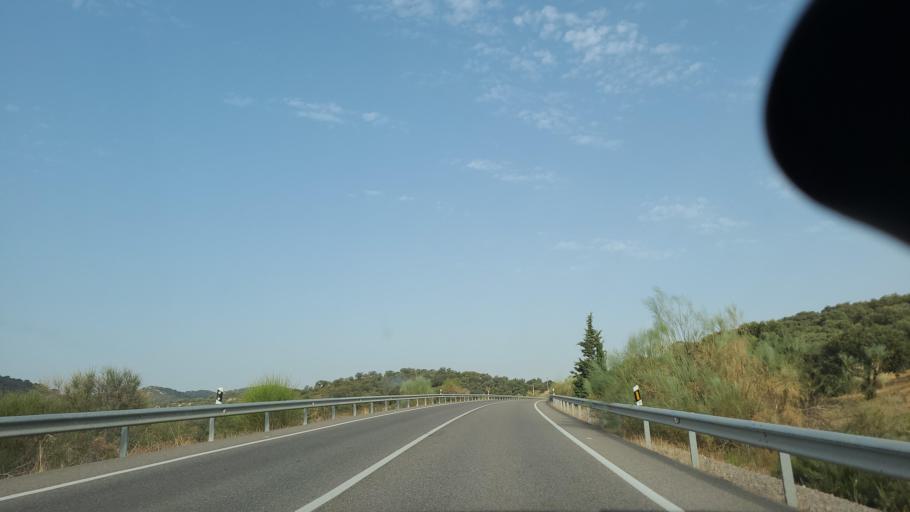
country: ES
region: Andalusia
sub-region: Province of Cordoba
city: Espiel
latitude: 38.1916
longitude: -5.0944
